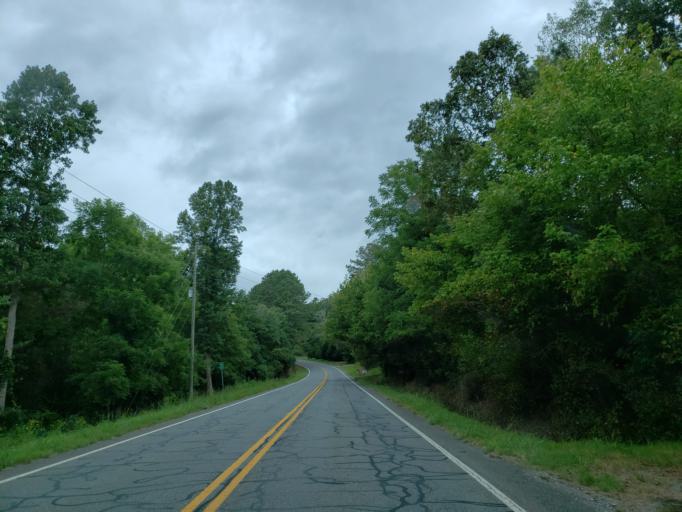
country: US
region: Georgia
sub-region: Gilmer County
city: Ellijay
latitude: 34.6398
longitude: -84.5745
